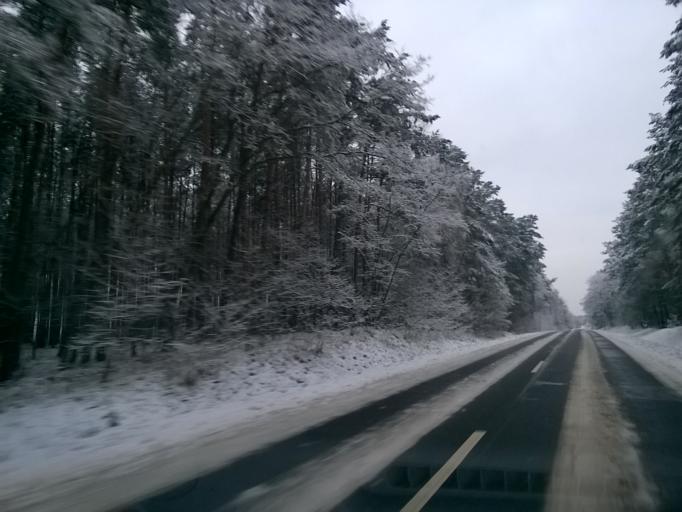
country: PL
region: Kujawsko-Pomorskie
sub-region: Powiat nakielski
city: Naklo nad Notecia
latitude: 53.0624
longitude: 17.5678
